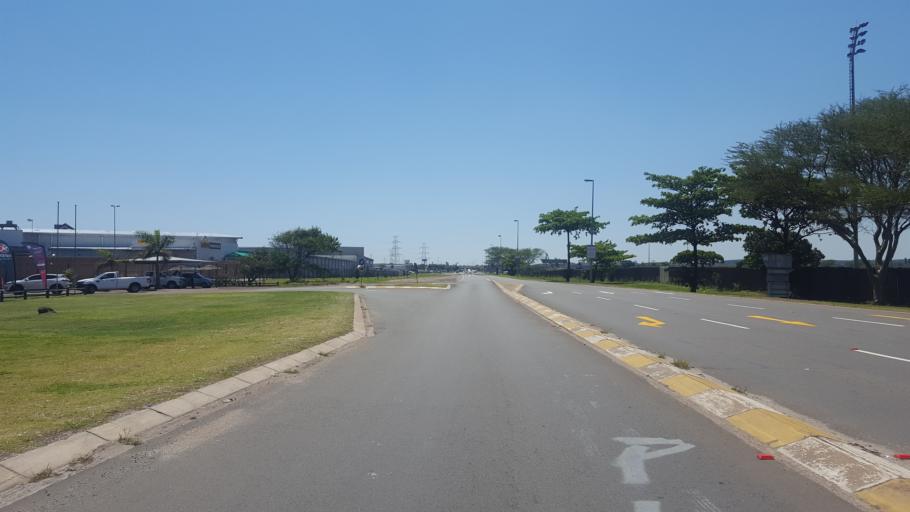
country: ZA
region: KwaZulu-Natal
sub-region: uThungulu District Municipality
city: Richards Bay
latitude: -28.7479
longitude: 32.0534
